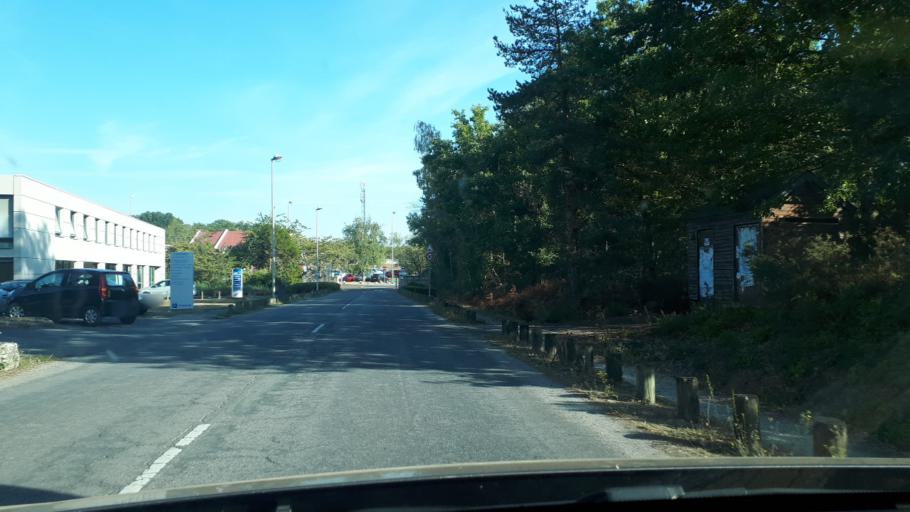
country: FR
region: Centre
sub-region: Departement du Loir-et-Cher
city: Naveil
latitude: 47.8201
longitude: 1.0218
